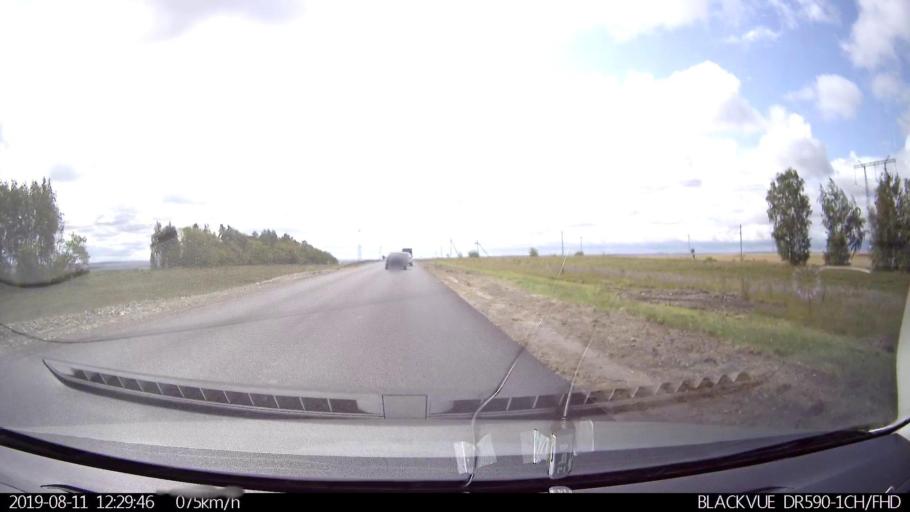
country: RU
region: Ulyanovsk
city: Ignatovka
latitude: 53.8317
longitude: 47.8996
